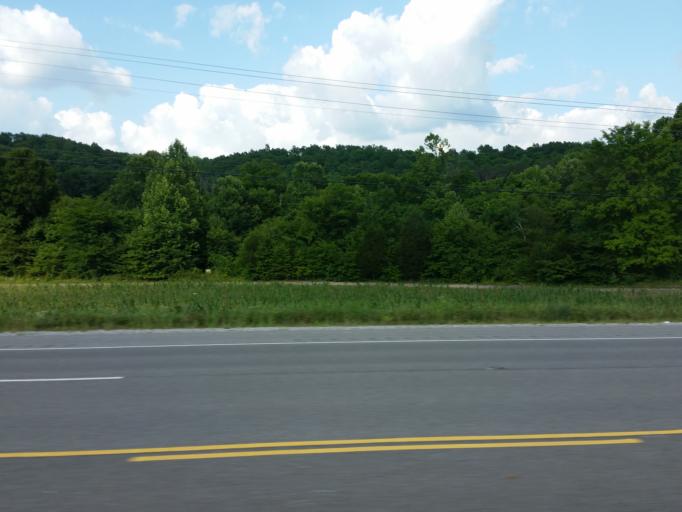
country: US
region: Tennessee
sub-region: Lewis County
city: Hohenwald
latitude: 35.5725
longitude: -87.4260
